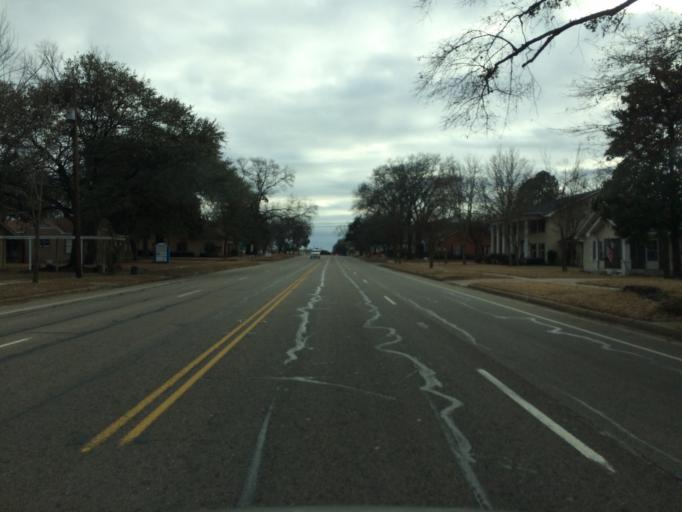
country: US
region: Texas
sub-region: Wood County
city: Mineola
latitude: 32.6682
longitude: -95.4866
